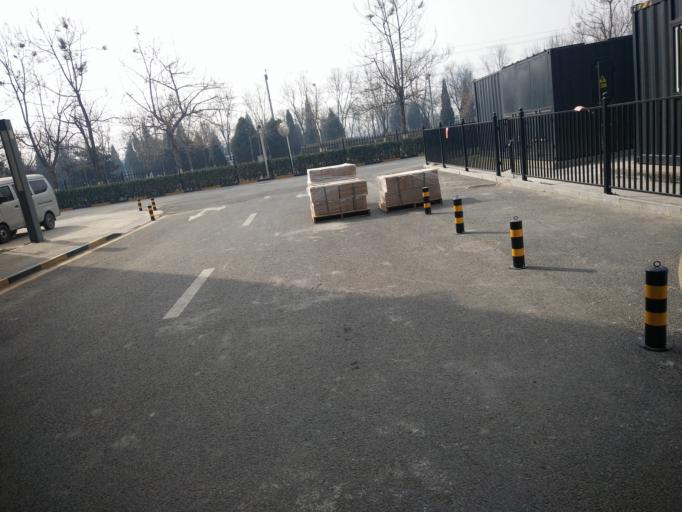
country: CN
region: Beijing
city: Jiugong
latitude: 39.7597
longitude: 116.5084
